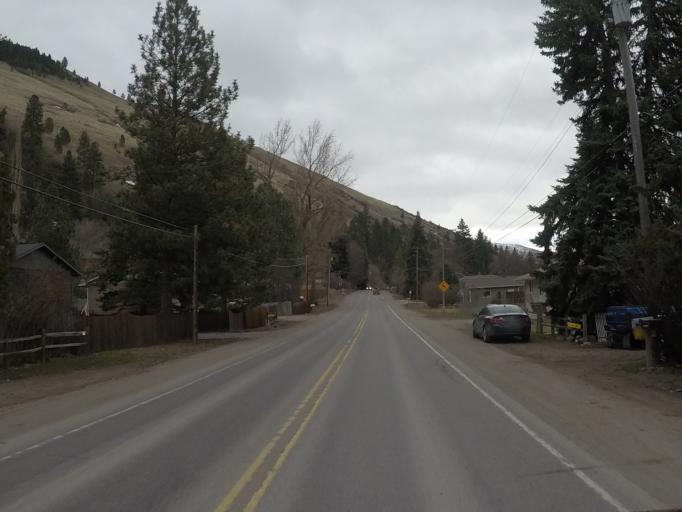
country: US
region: Montana
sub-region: Missoula County
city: Missoula
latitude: 46.8812
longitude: -113.9698
